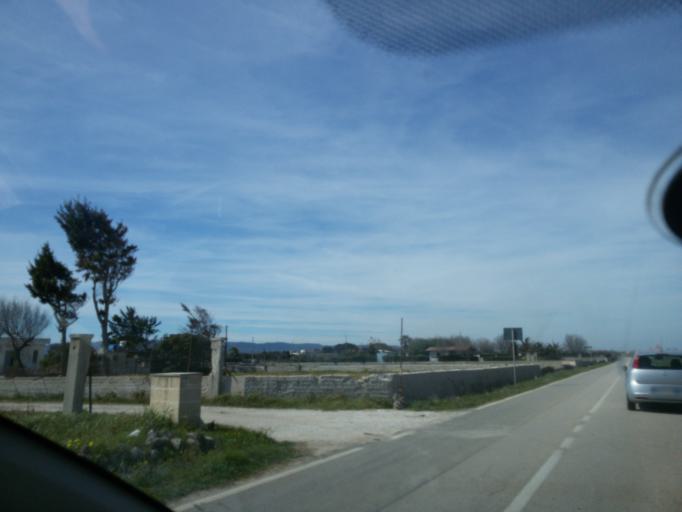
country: IT
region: Apulia
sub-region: Provincia di Brindisi
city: Pezze di Greco
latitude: 40.8449
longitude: 17.4617
